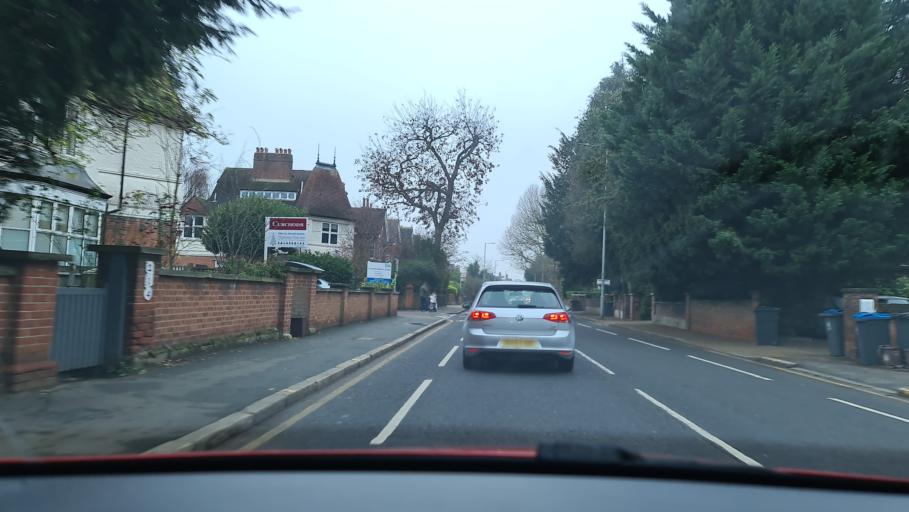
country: GB
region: England
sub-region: Greater London
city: Kingston upon Thames
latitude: 51.4218
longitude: -0.3027
